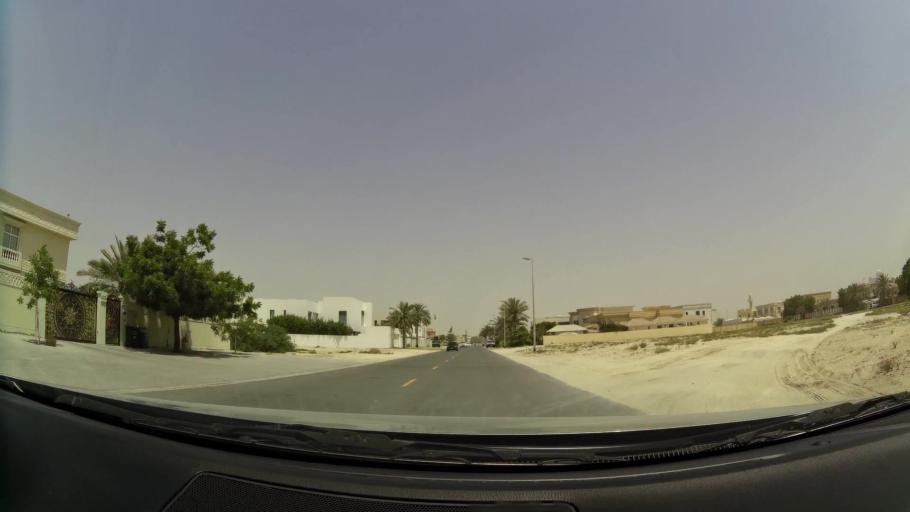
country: AE
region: Dubai
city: Dubai
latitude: 25.1351
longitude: 55.2028
